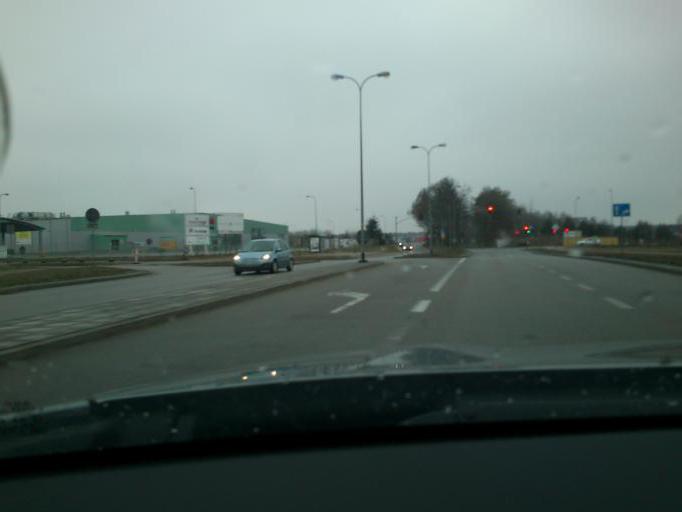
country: PL
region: Pomeranian Voivodeship
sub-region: Gdynia
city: Wielki Kack
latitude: 54.4134
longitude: 18.4809
